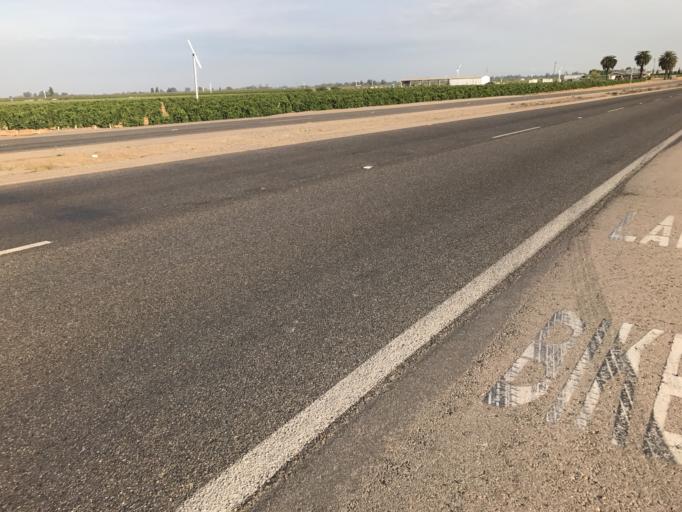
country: US
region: California
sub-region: Fresno County
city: Sanger
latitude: 36.7223
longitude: -119.5564
